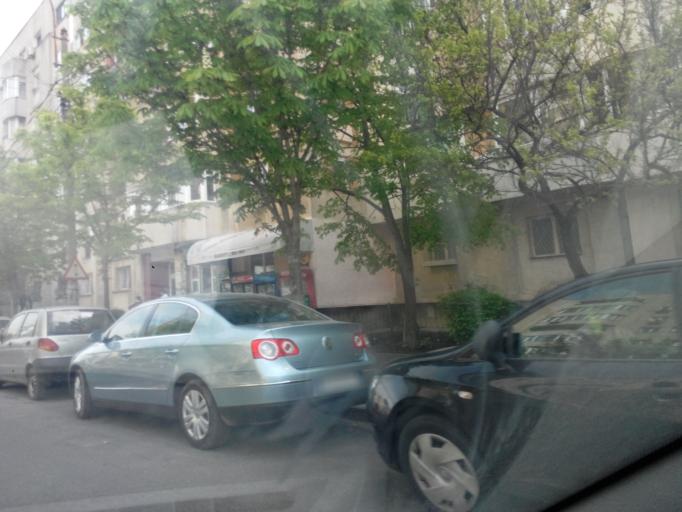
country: RO
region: Bucuresti
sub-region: Municipiul Bucuresti
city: Bucharest
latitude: 44.4310
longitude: 26.1291
